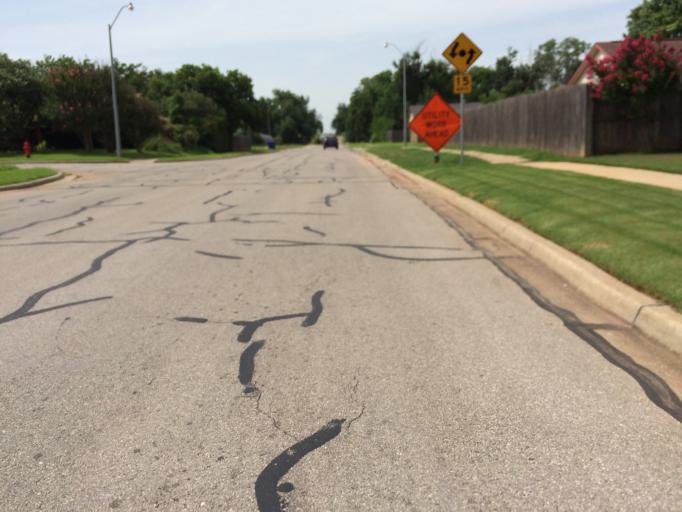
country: US
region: Oklahoma
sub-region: Cleveland County
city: Norman
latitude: 35.1924
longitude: -97.4104
